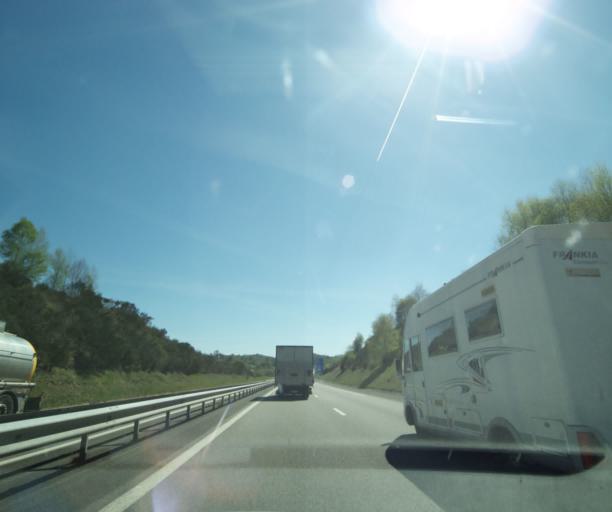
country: FR
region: Limousin
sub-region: Departement de la Correze
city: Vigeois
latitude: 45.3420
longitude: 1.5717
